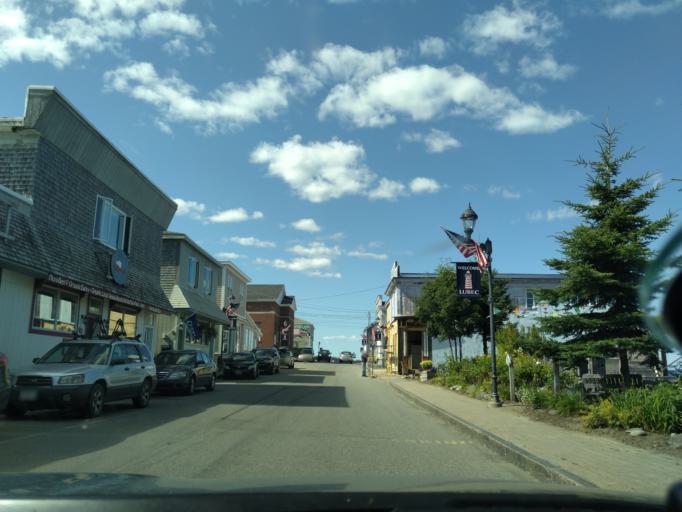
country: US
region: Maine
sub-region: Washington County
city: Eastport
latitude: 44.8608
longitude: -66.9833
